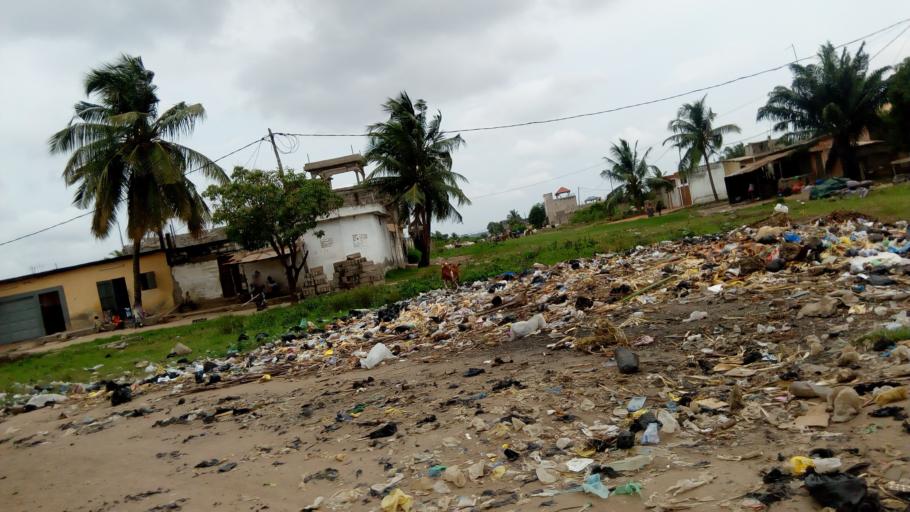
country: TG
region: Maritime
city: Lome
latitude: 6.2530
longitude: 1.2188
